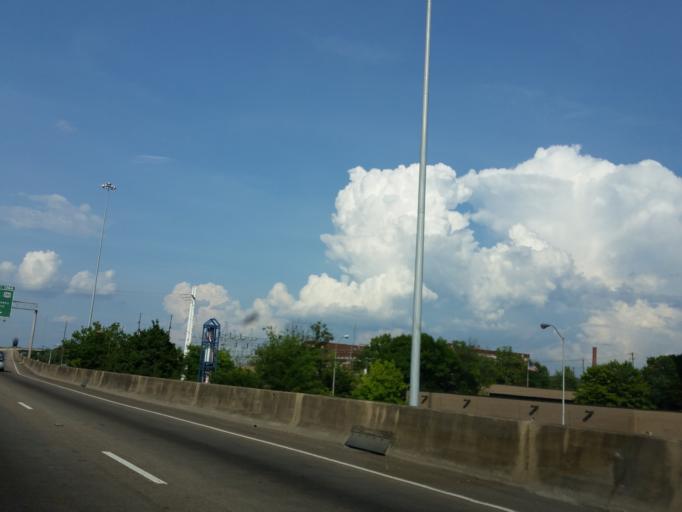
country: US
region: Alabama
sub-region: Jefferson County
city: Birmingham
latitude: 33.5237
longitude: -86.8082
